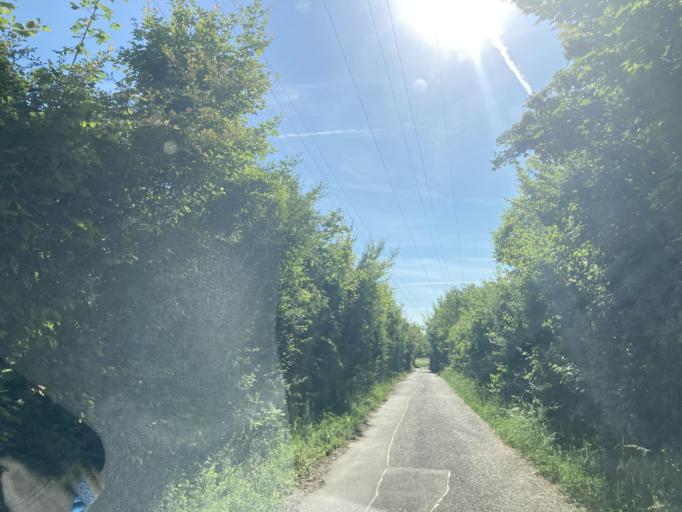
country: DE
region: Baden-Wuerttemberg
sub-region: Karlsruhe Region
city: Kronau
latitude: 49.2094
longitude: 8.6336
